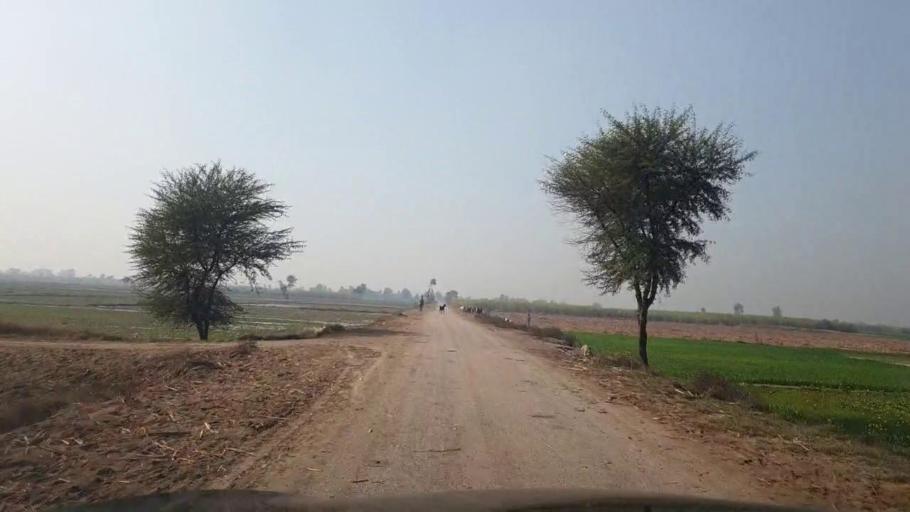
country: PK
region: Sindh
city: Ubauro
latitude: 28.1234
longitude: 69.8190
